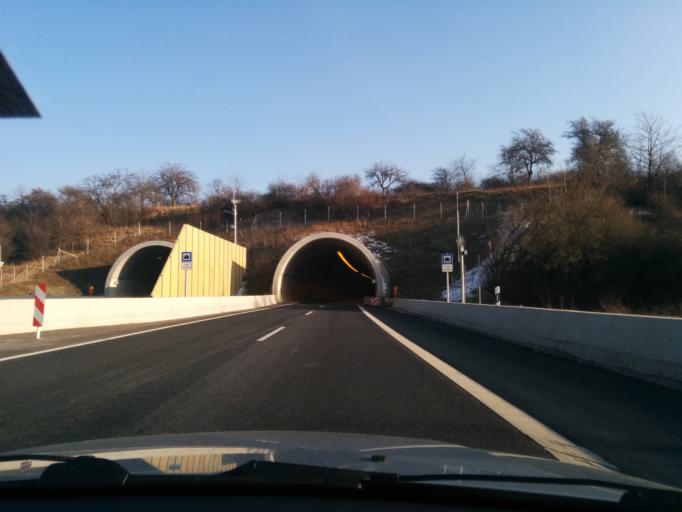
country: DE
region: Hesse
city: Hessisch Lichtenau
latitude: 51.2083
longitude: 9.7321
